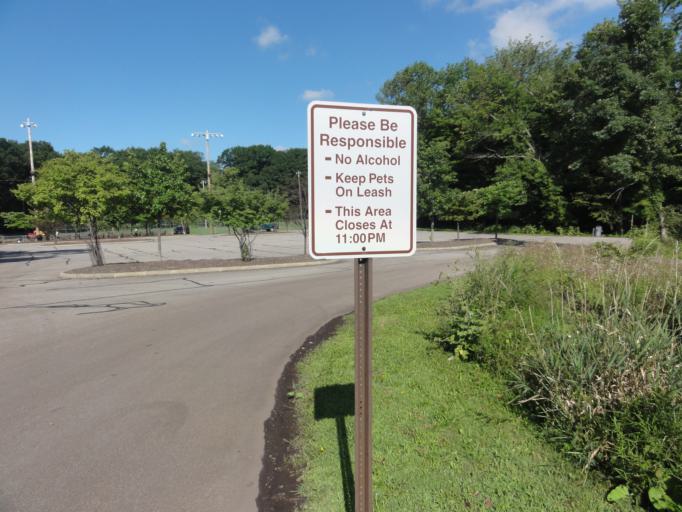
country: US
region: Ohio
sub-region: Cuyahoga County
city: Bedford
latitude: 41.3870
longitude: -81.5355
